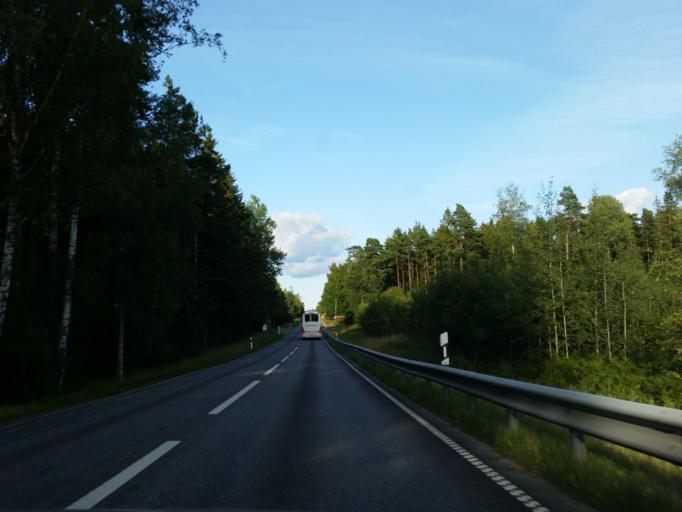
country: SE
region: Stockholm
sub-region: Sodertalje Kommun
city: Molnbo
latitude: 59.0384
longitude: 17.3807
